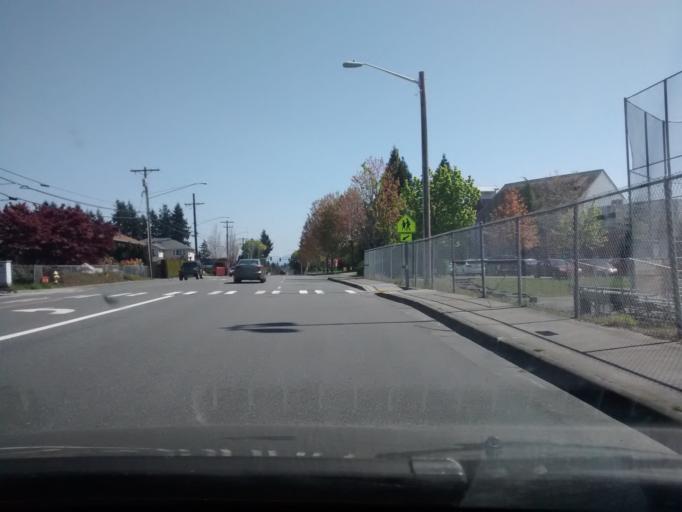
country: US
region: Washington
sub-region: Snohomish County
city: Esperance
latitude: 47.8069
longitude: -122.3391
